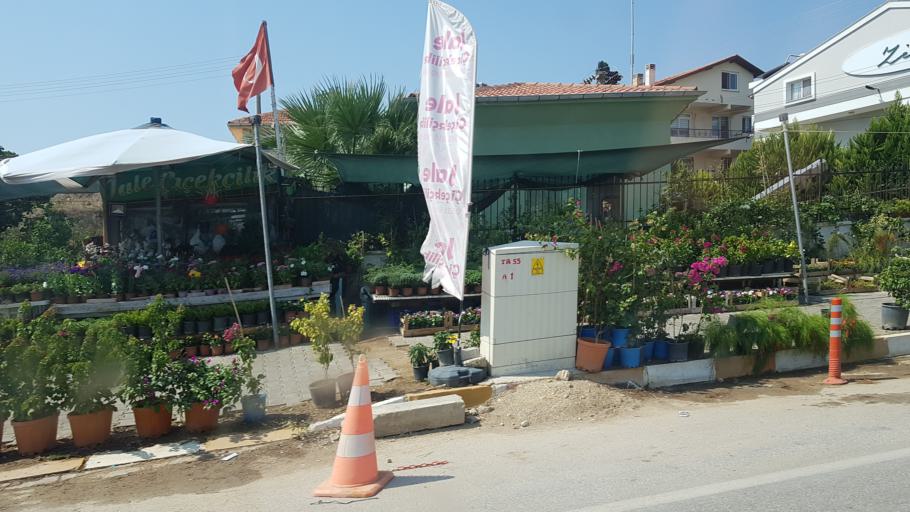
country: TR
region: Izmir
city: Urla
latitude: 38.3635
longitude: 26.7688
